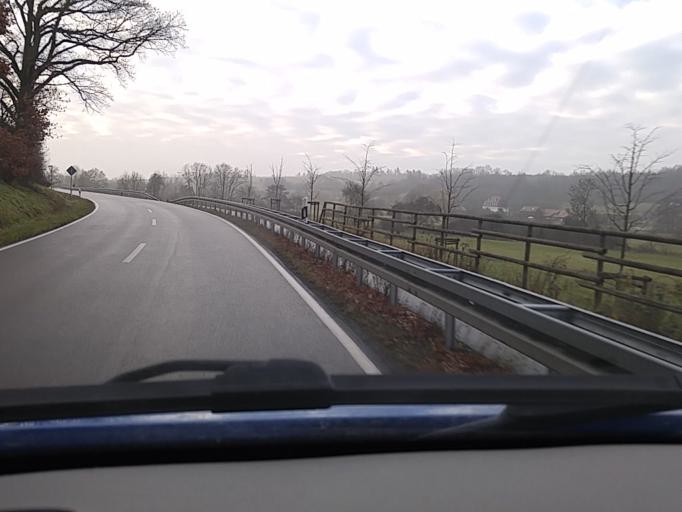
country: DE
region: Hesse
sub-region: Regierungsbezirk Darmstadt
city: Bad Nauheim
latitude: 50.3826
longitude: 8.7565
